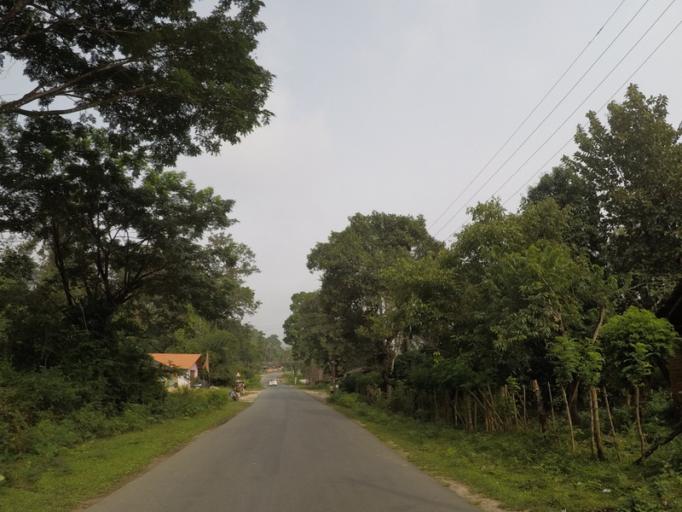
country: IN
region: Karnataka
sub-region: Chikmagalur
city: Chikmagalur
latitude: 13.3383
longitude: 75.5478
